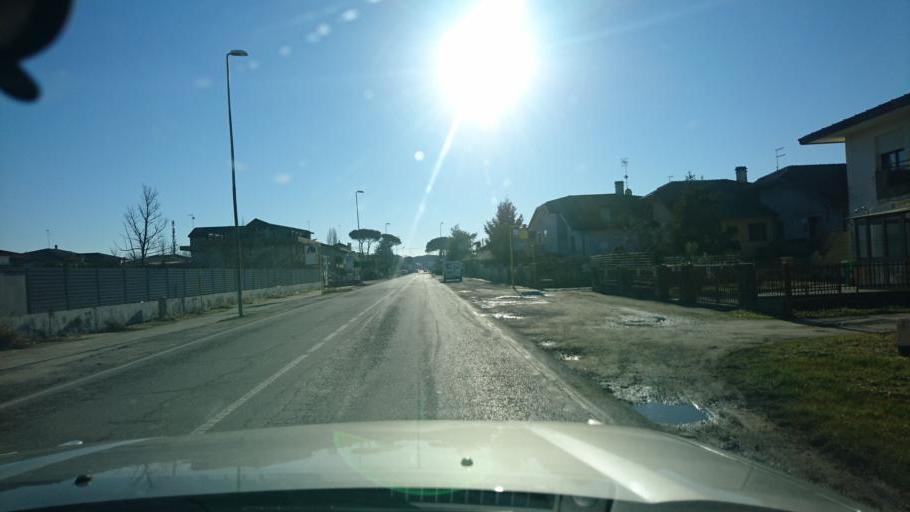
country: IT
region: Veneto
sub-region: Provincia di Rovigo
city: Porto Viro
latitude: 45.0451
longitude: 12.2139
